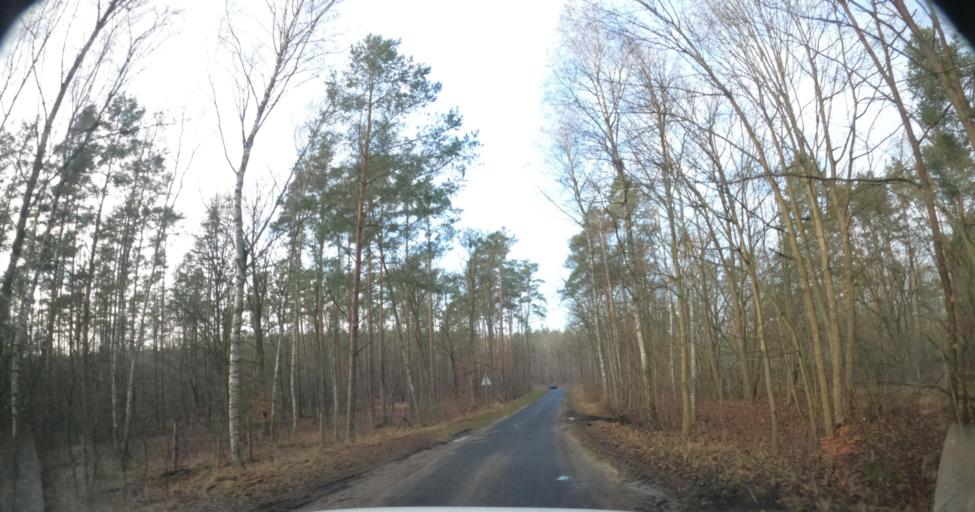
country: PL
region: West Pomeranian Voivodeship
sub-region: Powiat mysliborski
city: Boleszkowice
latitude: 52.7066
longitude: 14.5420
